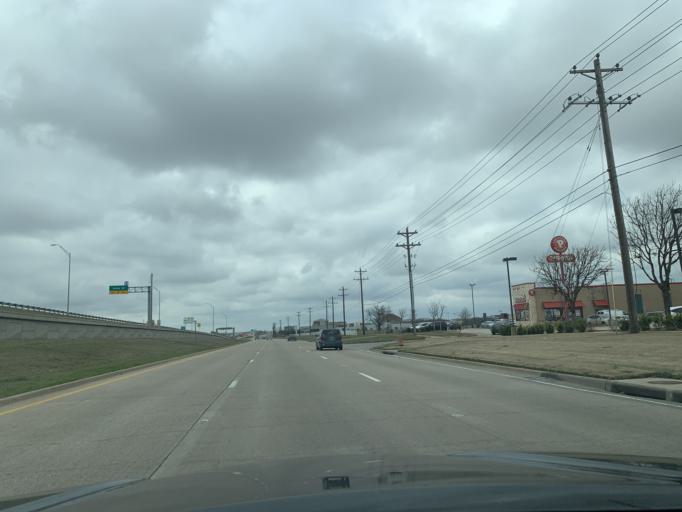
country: US
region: Texas
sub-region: Collin County
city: Allen
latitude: 33.1403
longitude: -96.6925
